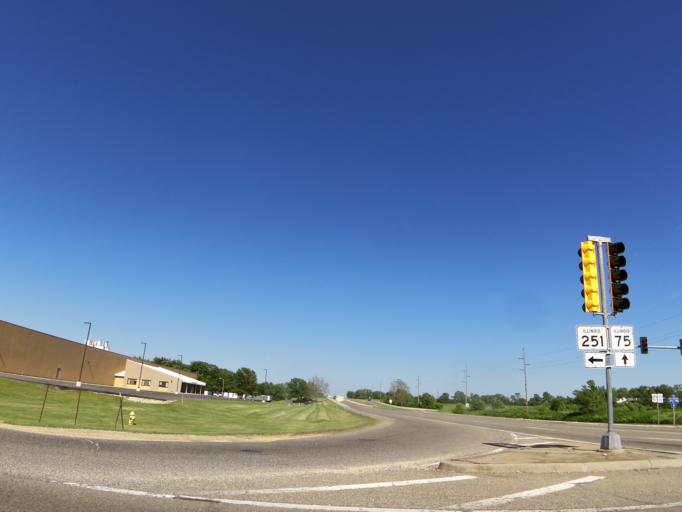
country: US
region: Illinois
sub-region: Winnebago County
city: South Beloit
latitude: 42.4922
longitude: -89.0196
